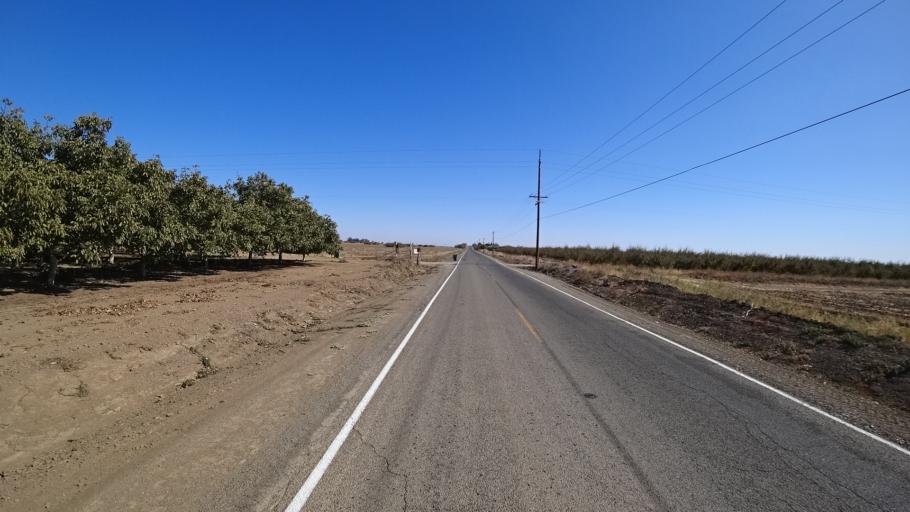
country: US
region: California
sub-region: Yolo County
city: Winters
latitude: 38.5618
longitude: -121.9626
